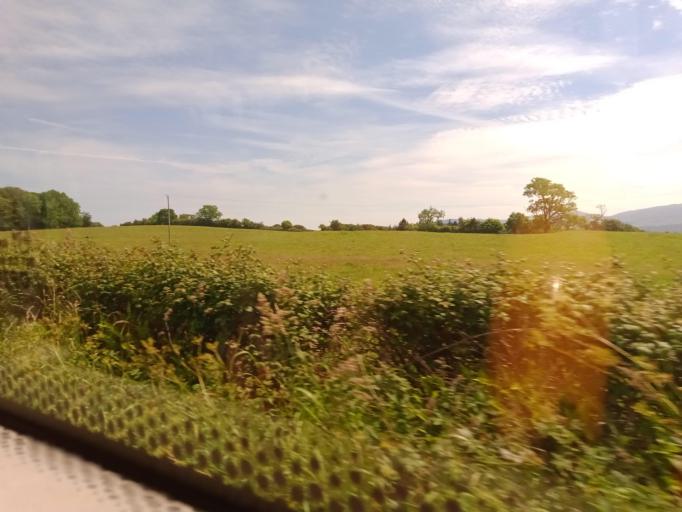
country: GB
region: Wales
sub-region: Anglesey
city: Beaumaris
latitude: 53.2641
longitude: -4.1165
